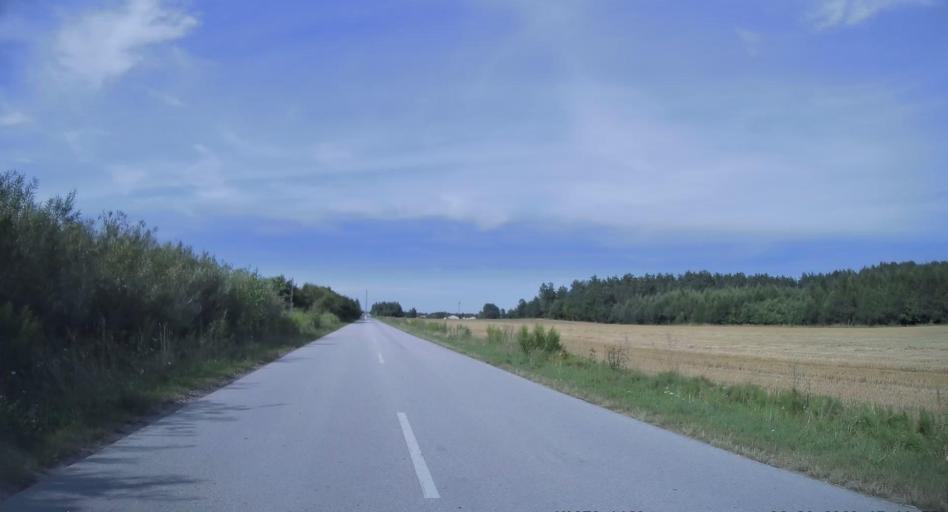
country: PL
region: Lodz Voivodeship
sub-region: Powiat opoczynski
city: Mniszkow
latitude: 51.3638
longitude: 20.0379
